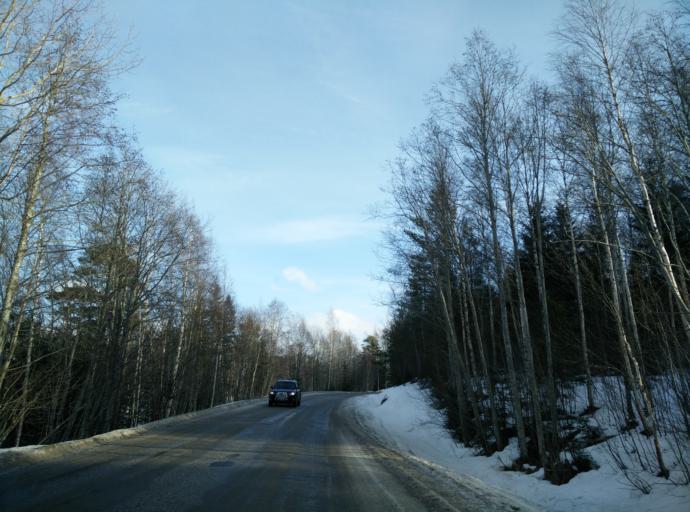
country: SE
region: Vaesternorrland
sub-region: Sundsvalls Kommun
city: Njurundabommen
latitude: 62.2210
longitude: 17.3446
